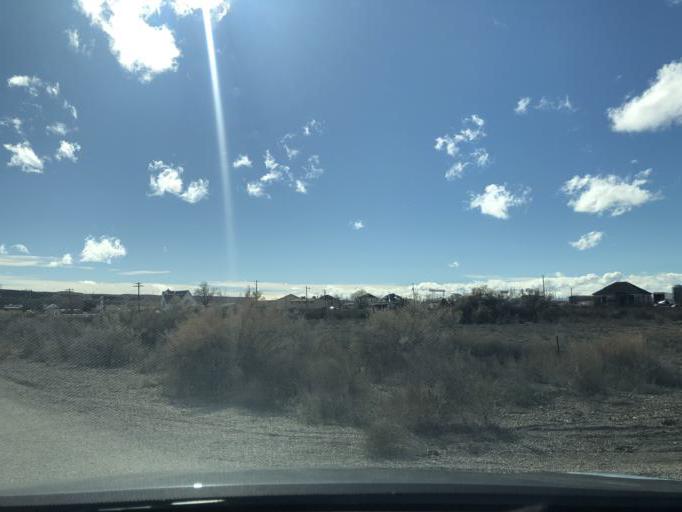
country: US
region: Utah
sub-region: Carbon County
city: East Carbon City
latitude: 38.9979
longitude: -110.1652
